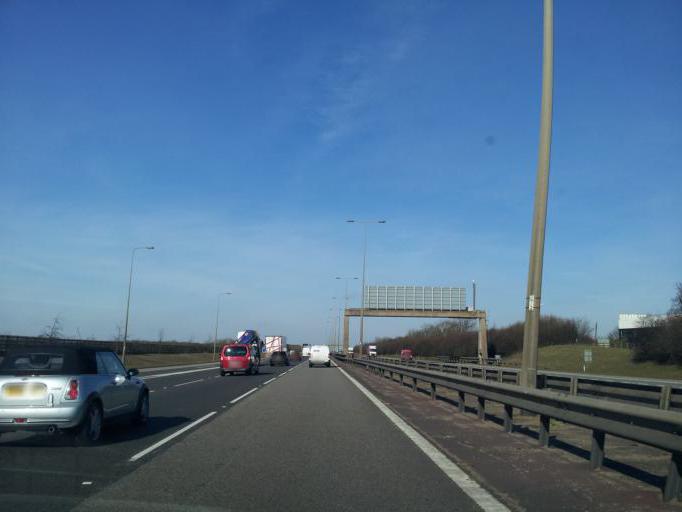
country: GB
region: England
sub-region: Cambridgeshire
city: Great Stukeley
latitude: 52.3879
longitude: -0.2586
